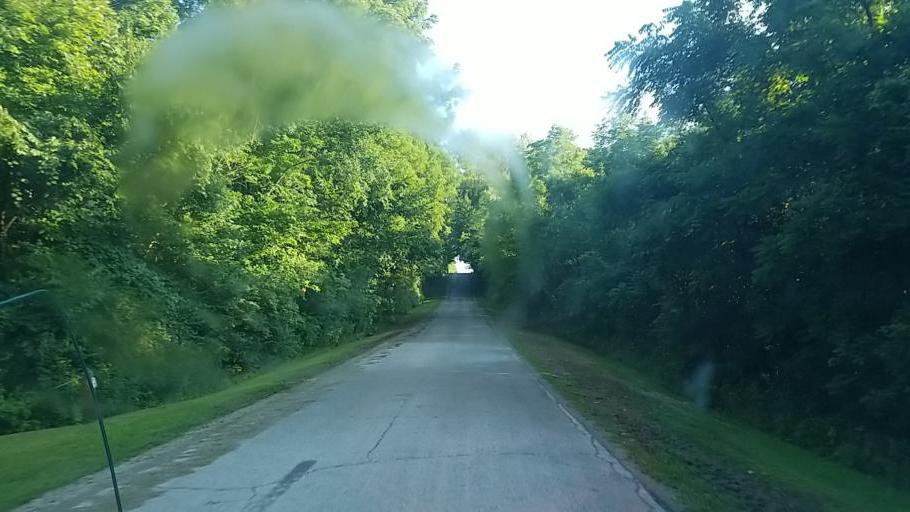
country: US
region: Ohio
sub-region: Crawford County
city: Bucyrus
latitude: 40.7682
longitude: -83.0551
